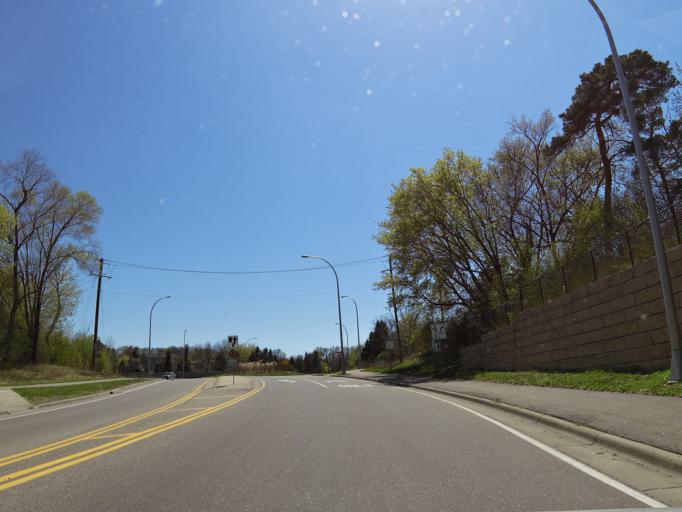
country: US
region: Minnesota
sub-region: Scott County
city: Savage
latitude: 44.7689
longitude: -93.3362
